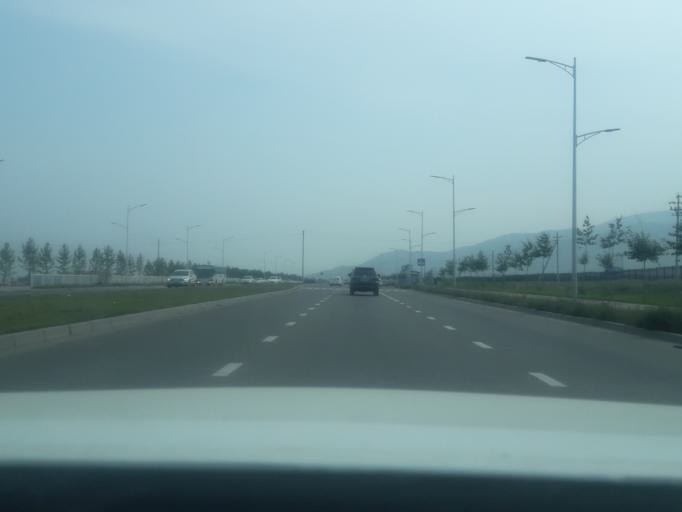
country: MN
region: Ulaanbaatar
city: Ulaanbaatar
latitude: 47.8649
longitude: 106.8103
